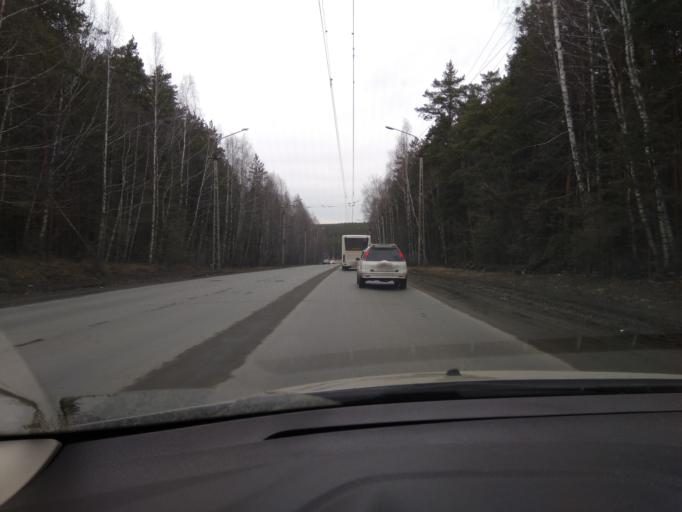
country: RU
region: Chelyabinsk
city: Turgoyak
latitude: 55.1251
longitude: 60.1337
